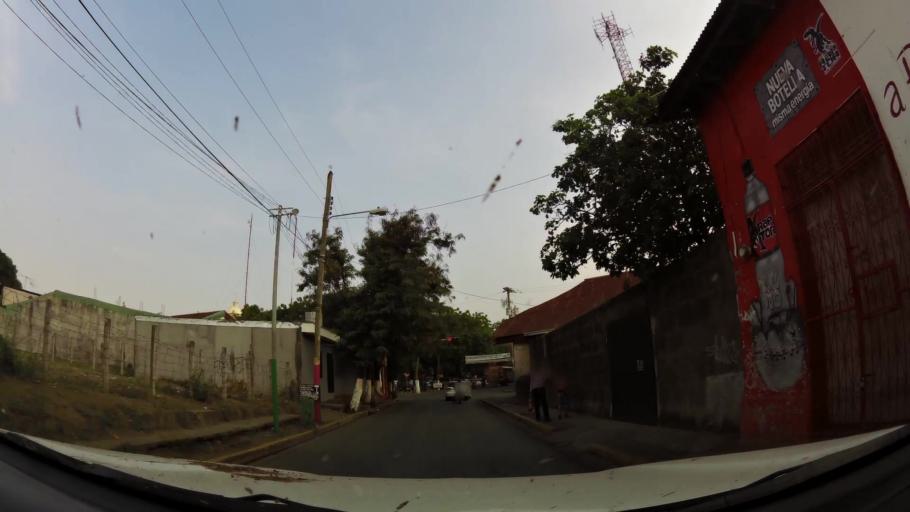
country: NI
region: Masaya
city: Masaya
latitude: 11.9746
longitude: -86.0972
